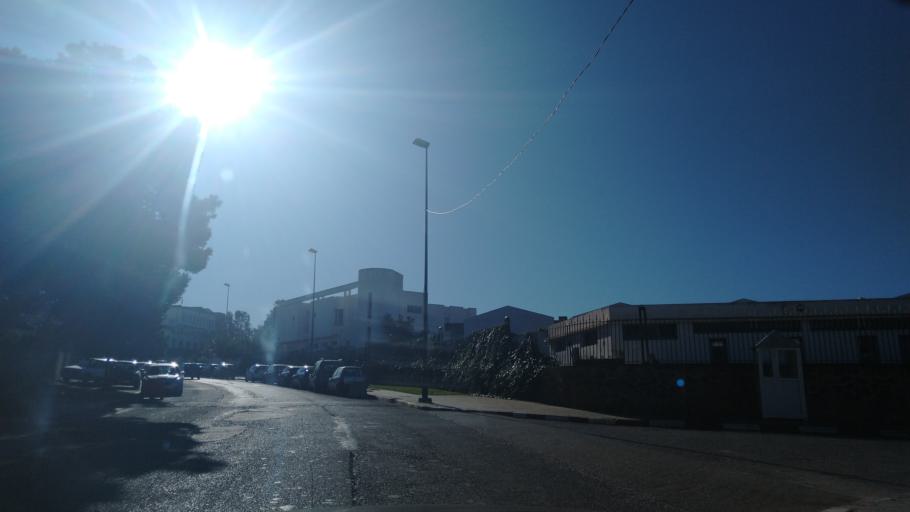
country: MA
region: Rabat-Sale-Zemmour-Zaer
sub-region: Rabat
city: Rabat
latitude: 33.9931
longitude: -6.8594
